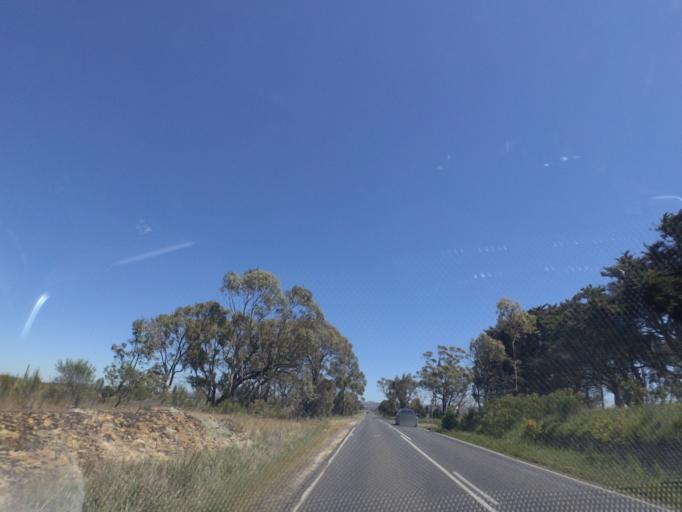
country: AU
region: Victoria
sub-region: Whittlesea
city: Whittlesea
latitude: -37.2915
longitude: 144.9102
